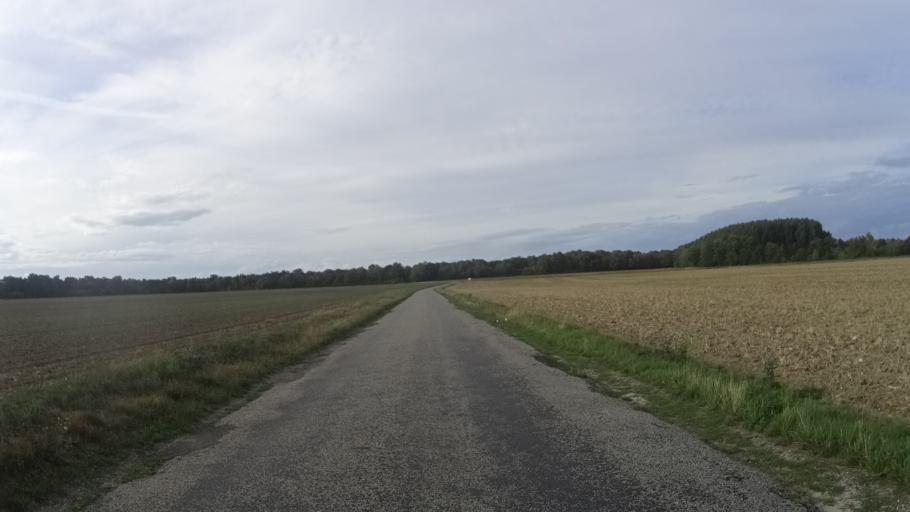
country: FR
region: Picardie
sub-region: Departement de l'Oise
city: Ver-sur-Launette
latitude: 49.1539
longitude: 2.6828
